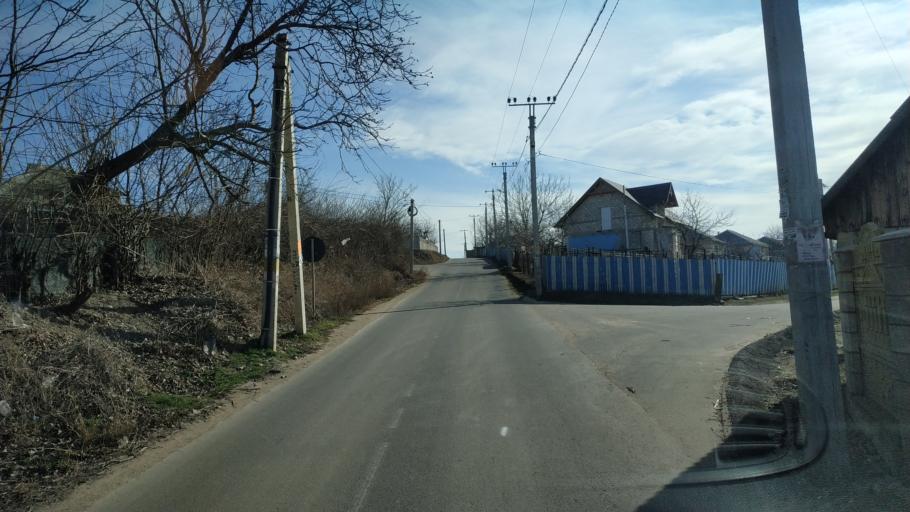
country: MD
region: Chisinau
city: Vatra
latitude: 47.0279
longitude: 28.6367
